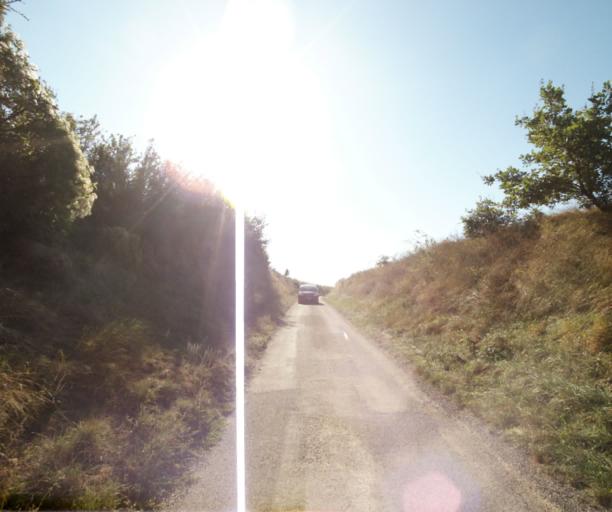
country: FR
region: Midi-Pyrenees
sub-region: Departement du Tarn-et-Garonne
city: Verdun-sur-Garonne
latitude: 43.8626
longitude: 1.2243
